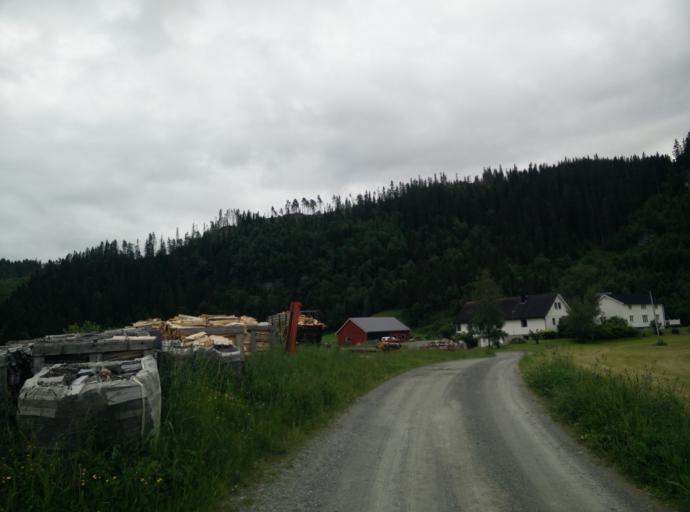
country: NO
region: Sor-Trondelag
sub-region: Skaun
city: Borsa
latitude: 63.3178
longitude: 10.0926
